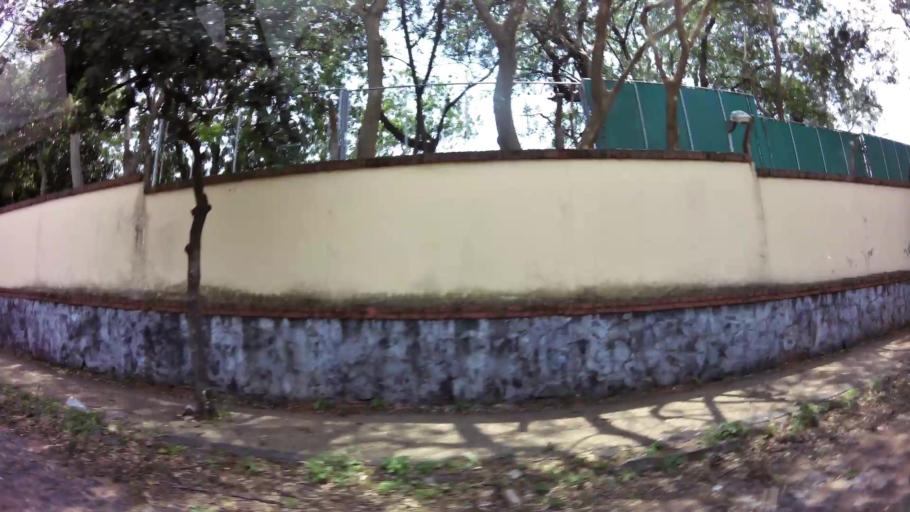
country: PY
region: Asuncion
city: Asuncion
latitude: -25.2969
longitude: -57.6031
